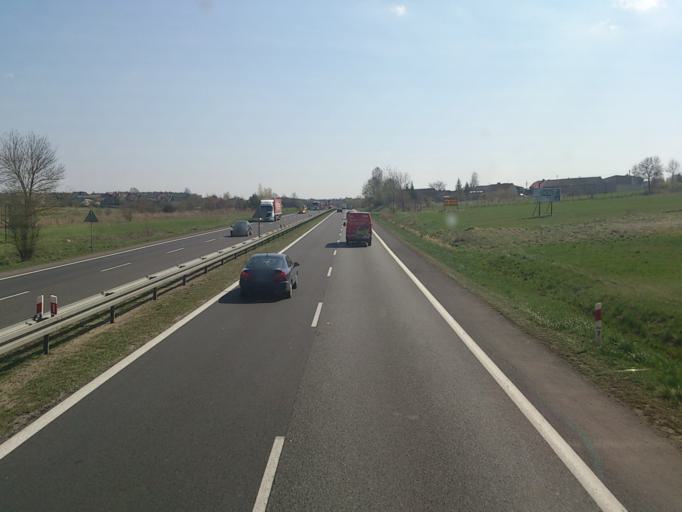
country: PL
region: Silesian Voivodeship
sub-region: Powiat myszkowski
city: Kozieglowy
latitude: 50.5751
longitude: 19.1634
